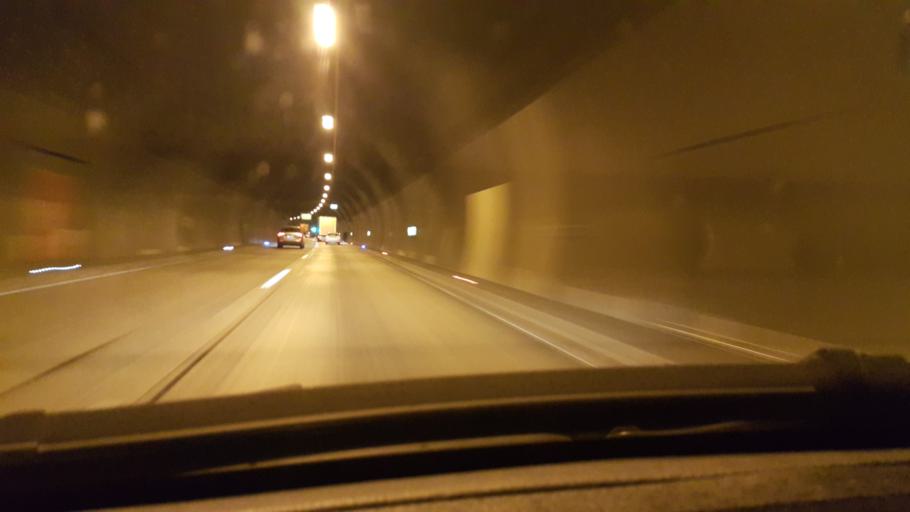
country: SI
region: Zagorje ob Savi
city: Izlake
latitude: 46.1881
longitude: 14.8860
